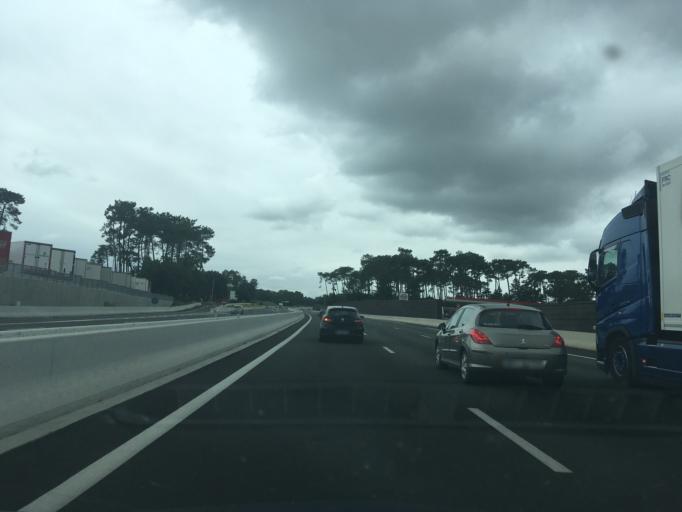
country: FR
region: Aquitaine
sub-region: Departement des Landes
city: Labenne
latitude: 43.5883
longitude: -1.4194
